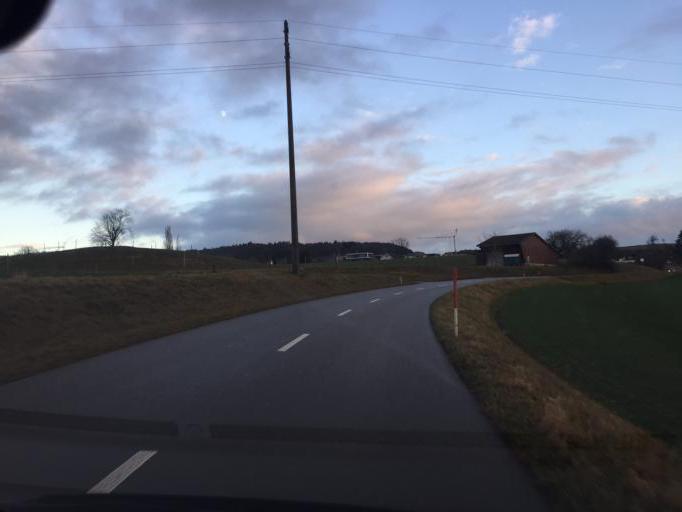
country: DE
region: Baden-Wuerttemberg
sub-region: Freiburg Region
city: Busingen
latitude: 47.7110
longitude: 8.7151
